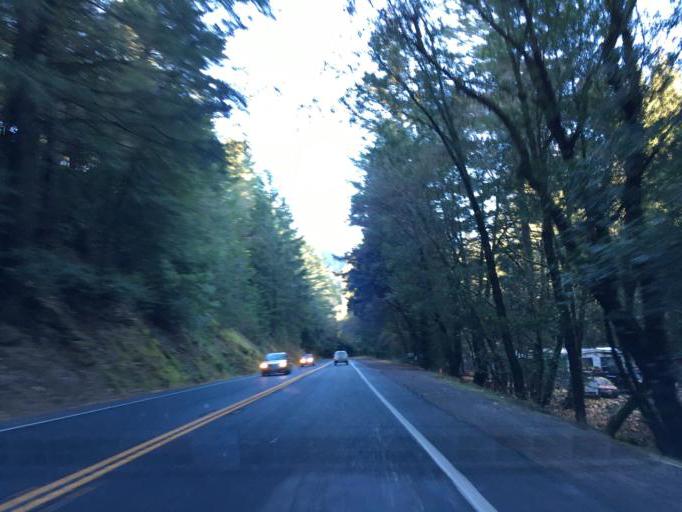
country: US
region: California
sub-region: Mendocino County
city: Brooktrails
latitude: 39.4984
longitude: -123.3716
